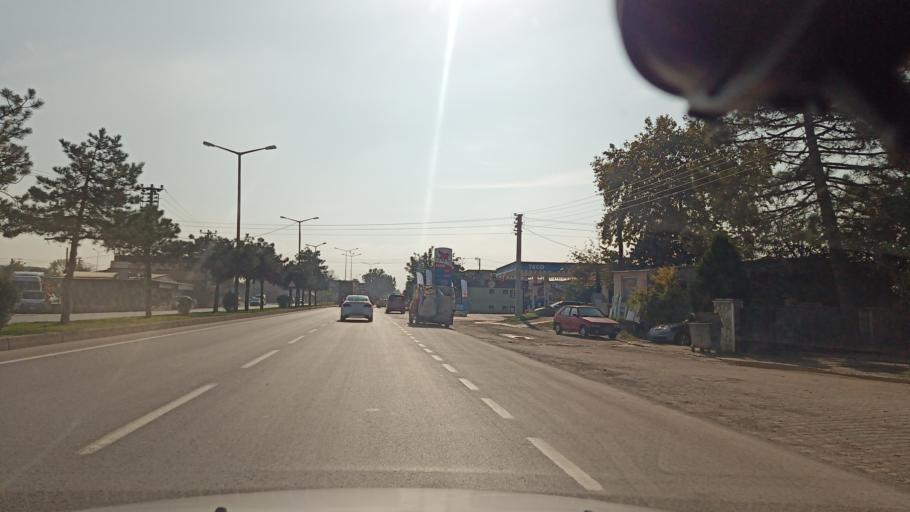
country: TR
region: Sakarya
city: Adapazari
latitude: 40.8022
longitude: 30.4062
